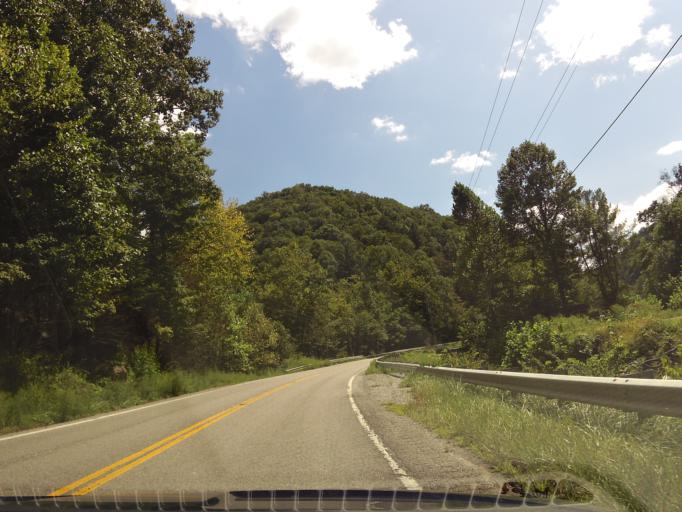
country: US
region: Kentucky
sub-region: Harlan County
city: Loyall
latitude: 36.9361
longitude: -83.3769
